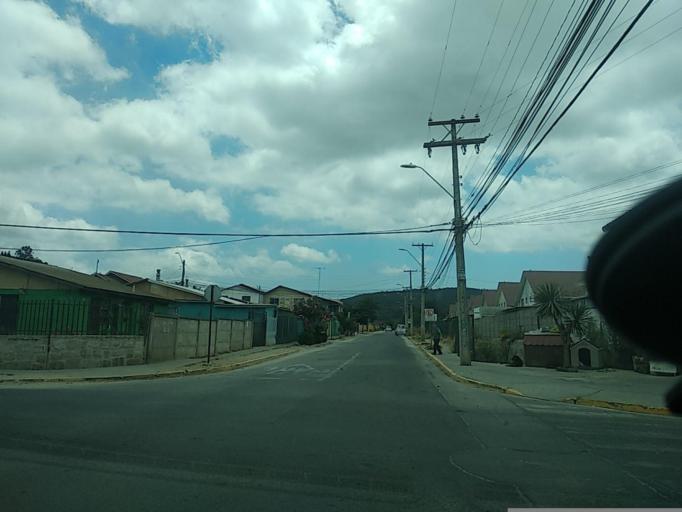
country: CL
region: Valparaiso
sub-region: Provincia de Marga Marga
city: Villa Alemana
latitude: -33.0321
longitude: -71.4063
